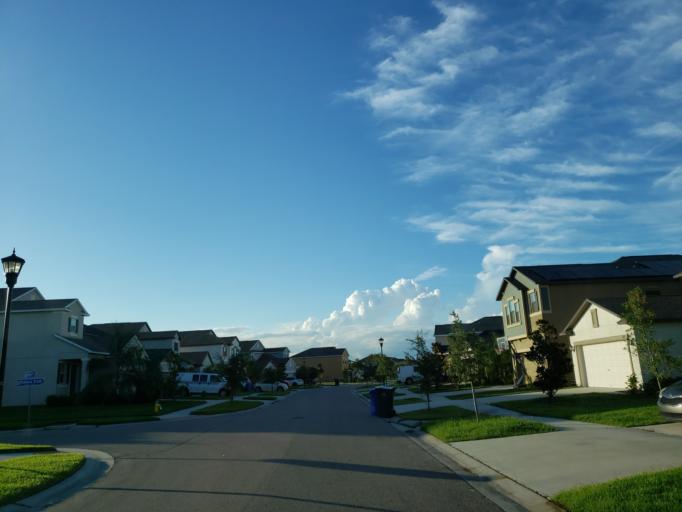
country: US
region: Florida
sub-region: Hillsborough County
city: Ruskin
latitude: 27.7296
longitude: -82.4082
